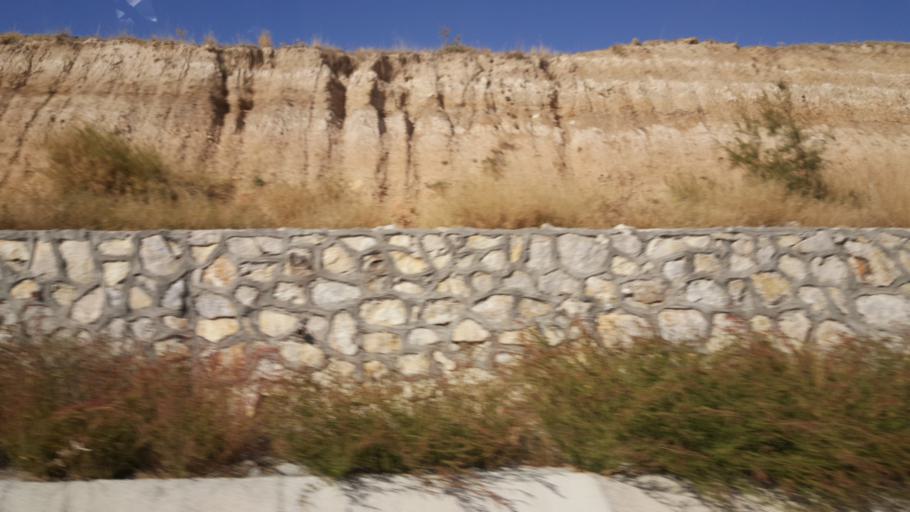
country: TR
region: Ankara
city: Ikizce
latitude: 39.5927
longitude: 32.6694
